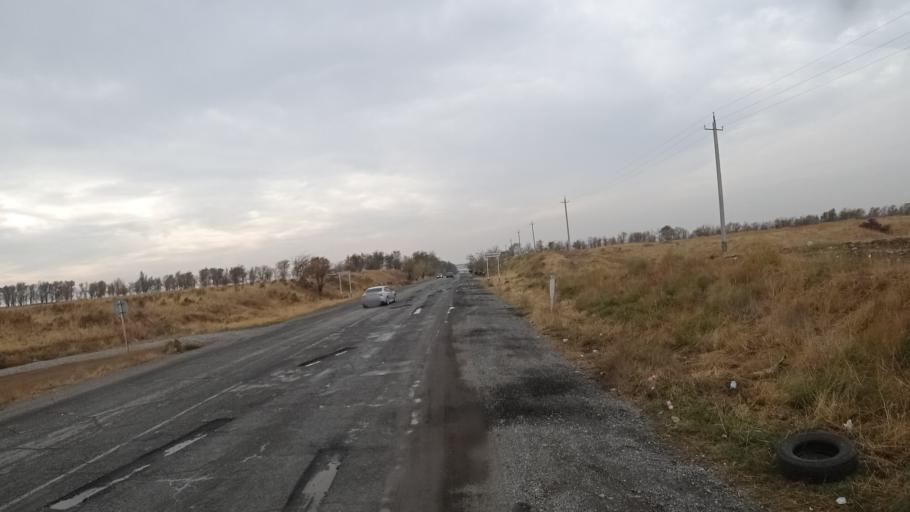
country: KZ
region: Ongtustik Qazaqstan
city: Aksu
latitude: 42.4321
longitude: 69.7126
